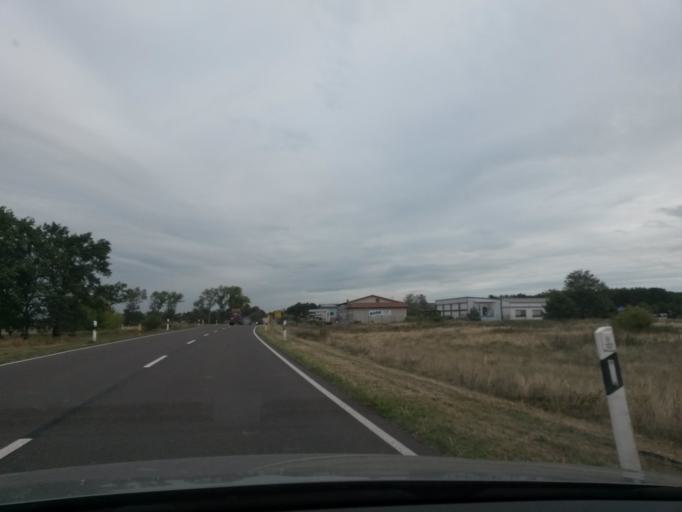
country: DE
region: Saxony-Anhalt
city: Schonhausen
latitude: 52.5713
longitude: 12.0325
